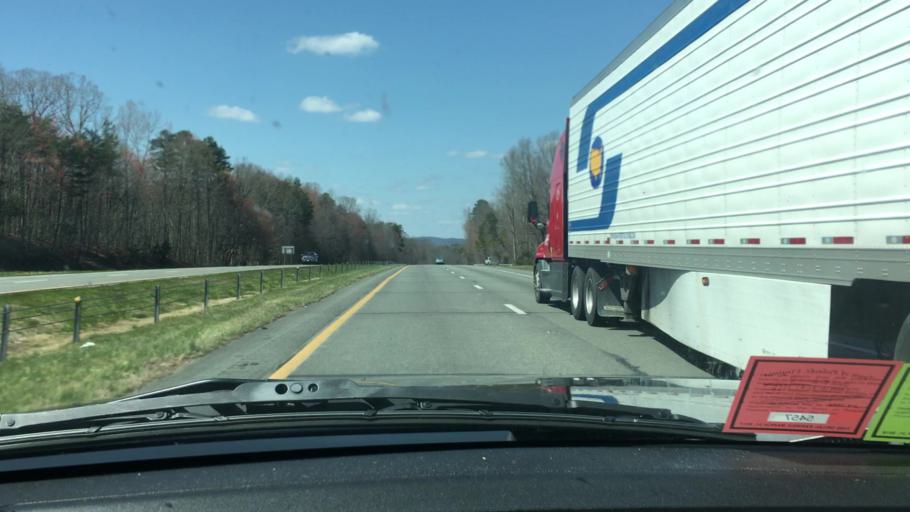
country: US
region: North Carolina
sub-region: Surry County
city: Pilot Mountain
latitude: 36.3772
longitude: -80.4868
